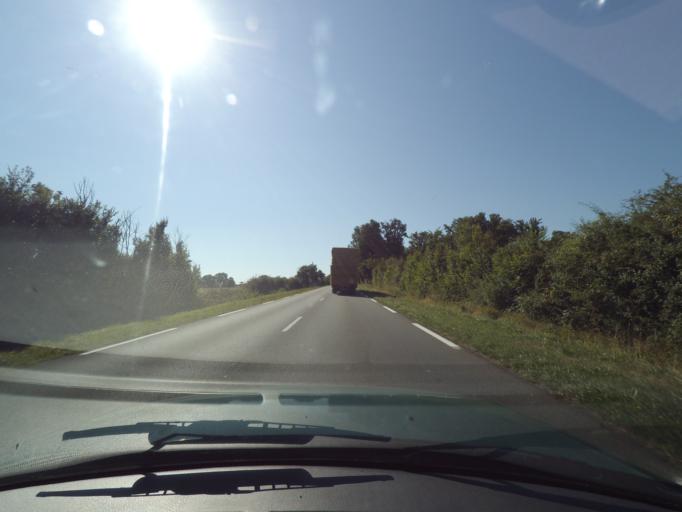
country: FR
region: Poitou-Charentes
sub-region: Departement de la Vienne
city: Lussac-les-Chateaux
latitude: 46.3903
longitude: 0.7393
